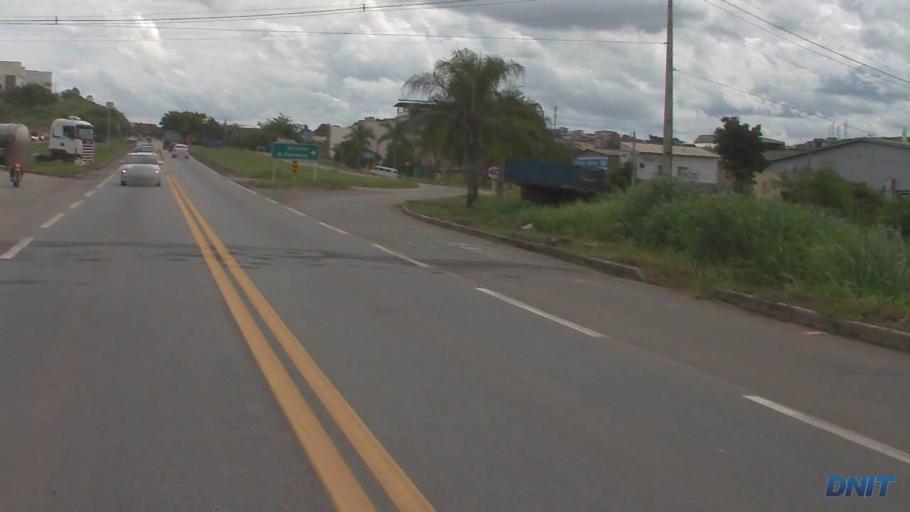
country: BR
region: Minas Gerais
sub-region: Ipatinga
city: Ipatinga
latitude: -19.4541
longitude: -42.5215
